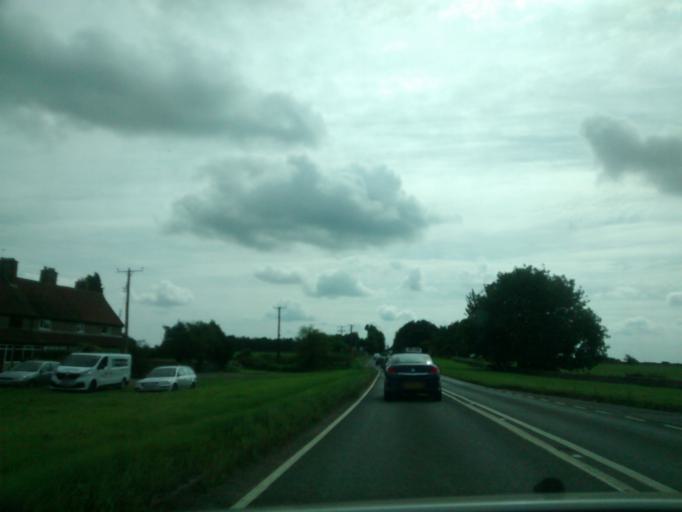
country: GB
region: England
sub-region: South Gloucestershire
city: Cold Ashton
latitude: 51.4157
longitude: -2.3947
